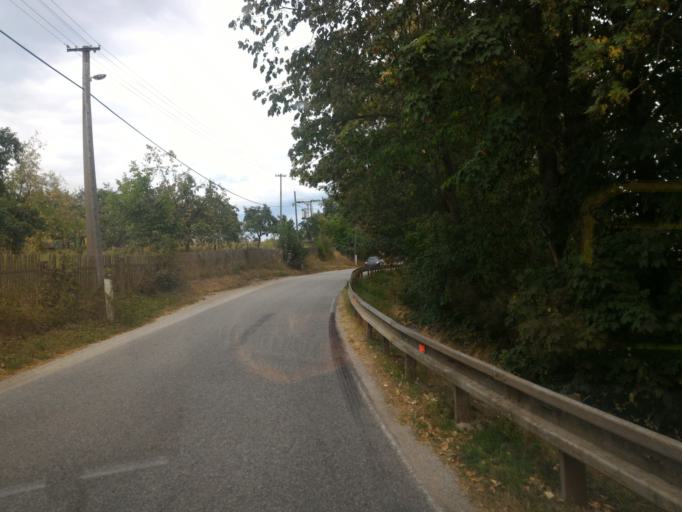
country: CZ
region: Vysocina
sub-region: Okres Jihlava
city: Telc
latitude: 49.1237
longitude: 15.5400
